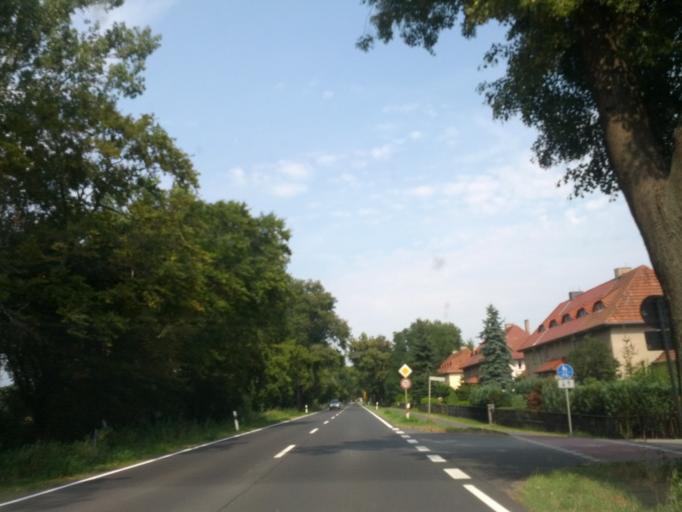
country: DE
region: Brandenburg
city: Nauen
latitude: 52.6266
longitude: 12.8992
